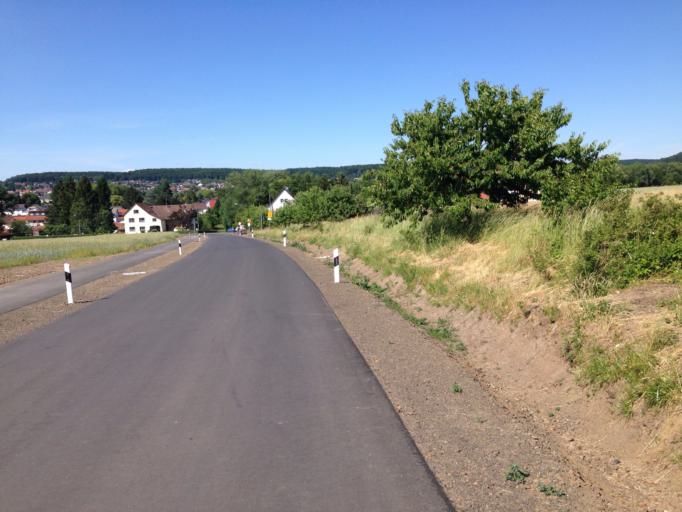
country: DE
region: Hesse
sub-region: Regierungsbezirk Giessen
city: Alten Buseck
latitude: 50.6060
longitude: 8.7535
